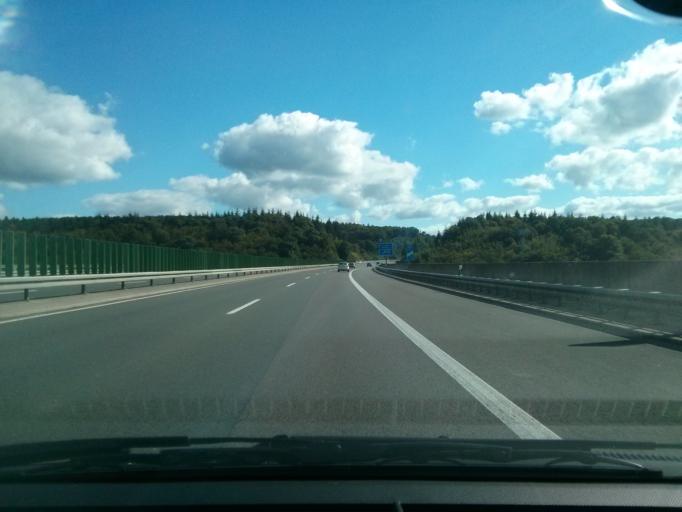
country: DE
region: North Rhine-Westphalia
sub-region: Regierungsbezirk Arnsberg
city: Arnsberg
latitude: 51.4275
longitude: 8.0527
